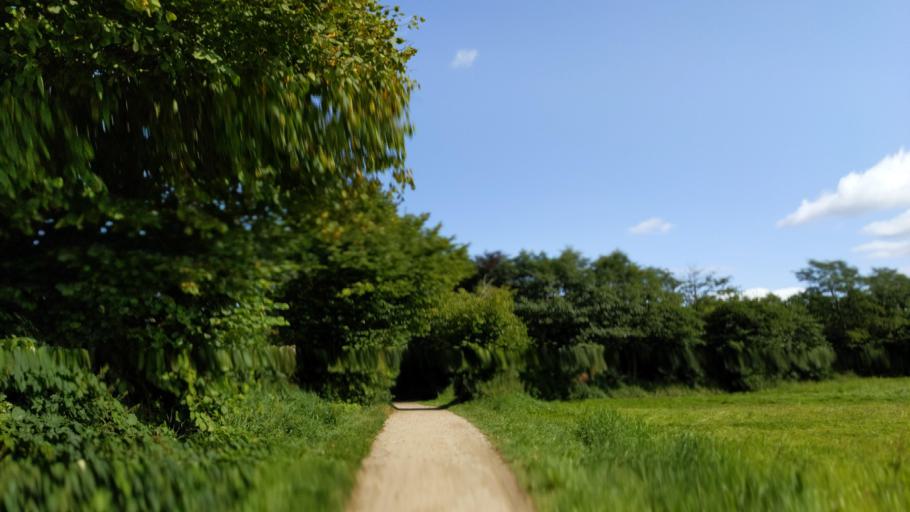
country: DE
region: Schleswig-Holstein
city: Eutin
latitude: 54.1481
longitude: 10.6135
